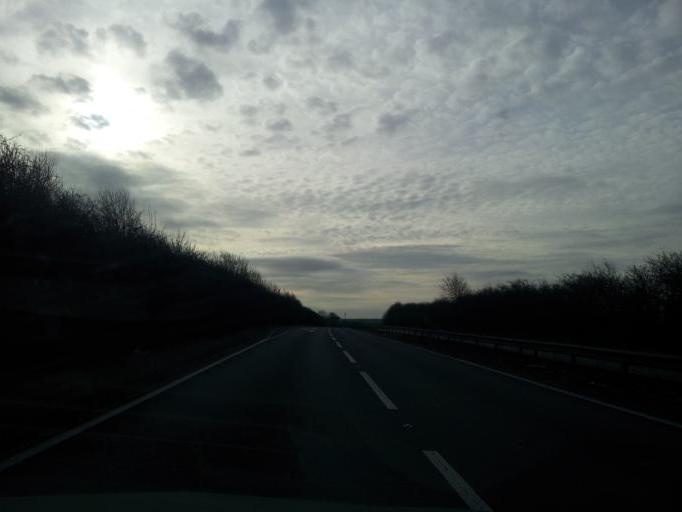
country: GB
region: England
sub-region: District of Rutland
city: Tinwell
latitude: 52.6590
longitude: -0.5167
